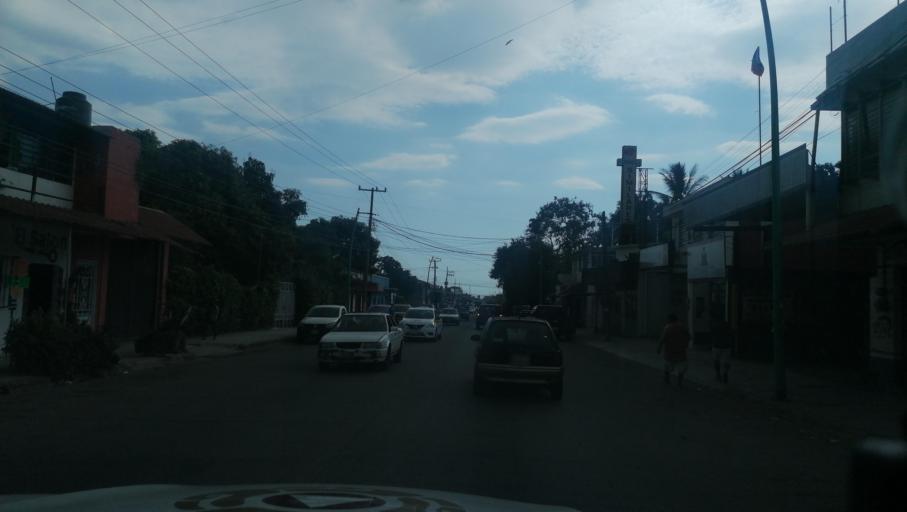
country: MX
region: Chiapas
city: Tapachula
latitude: 14.9252
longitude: -92.2537
